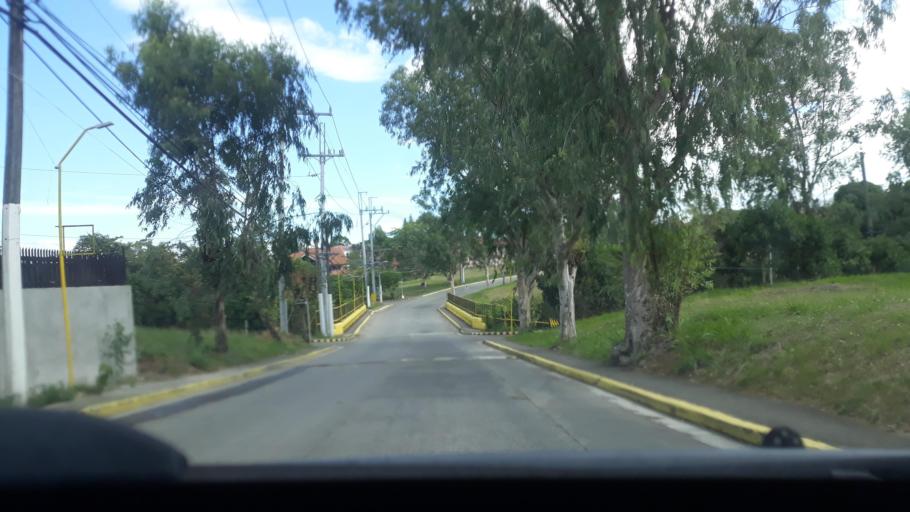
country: PH
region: Calabarzon
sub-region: Province of Cavite
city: Bulihan
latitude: 14.3028
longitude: 120.9666
